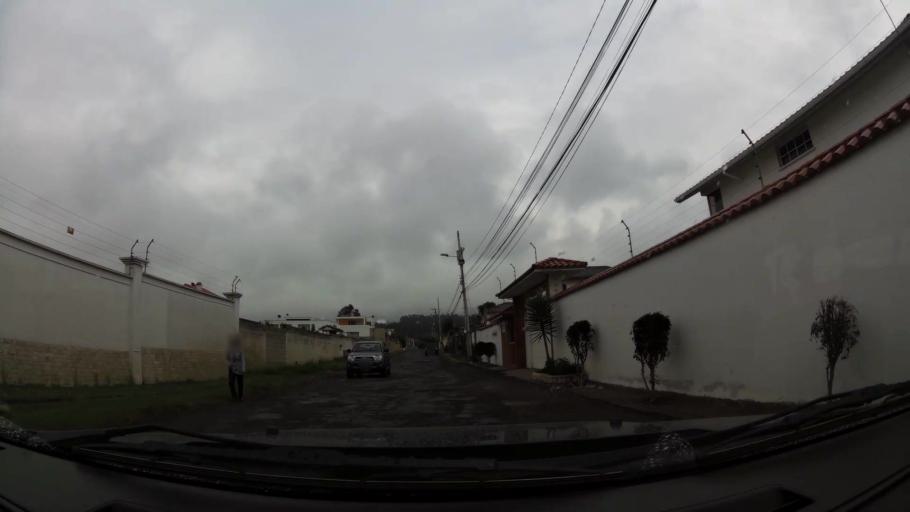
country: EC
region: Pichincha
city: Sangolqui
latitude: -0.2722
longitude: -78.4620
